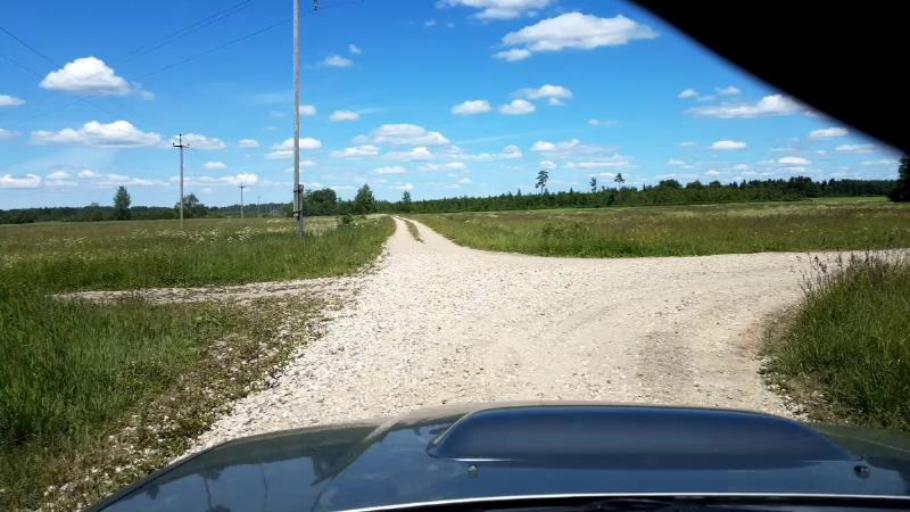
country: EE
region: Paernumaa
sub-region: Halinga vald
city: Parnu-Jaagupi
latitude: 58.5334
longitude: 24.5295
